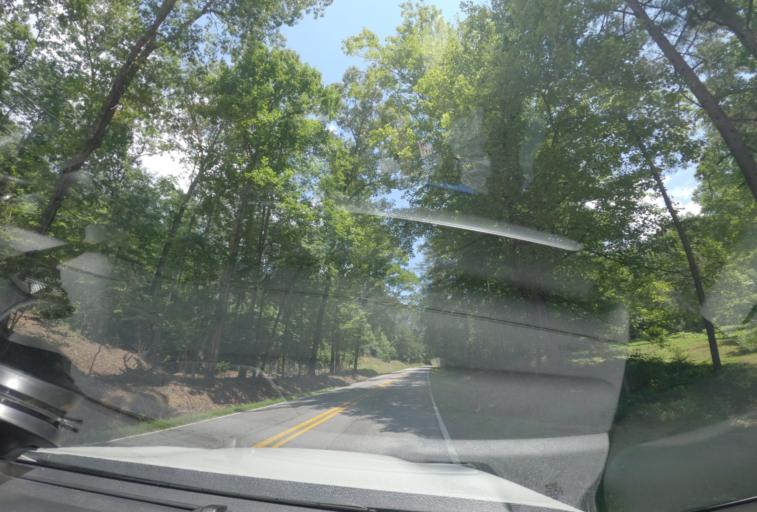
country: US
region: South Carolina
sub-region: Pickens County
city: Pickens
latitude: 34.9668
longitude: -82.8671
